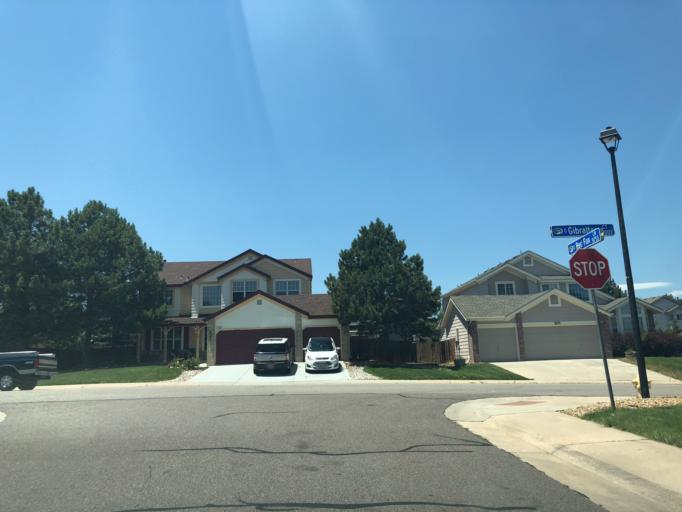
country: US
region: Colorado
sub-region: Arapahoe County
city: Dove Valley
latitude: 39.6222
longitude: -104.7556
